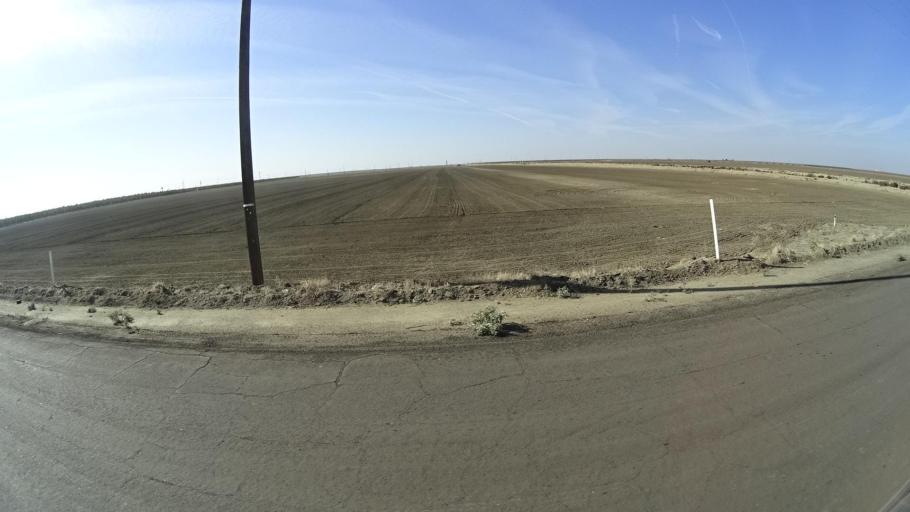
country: US
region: California
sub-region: Kern County
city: Wasco
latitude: 35.6802
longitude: -119.3840
